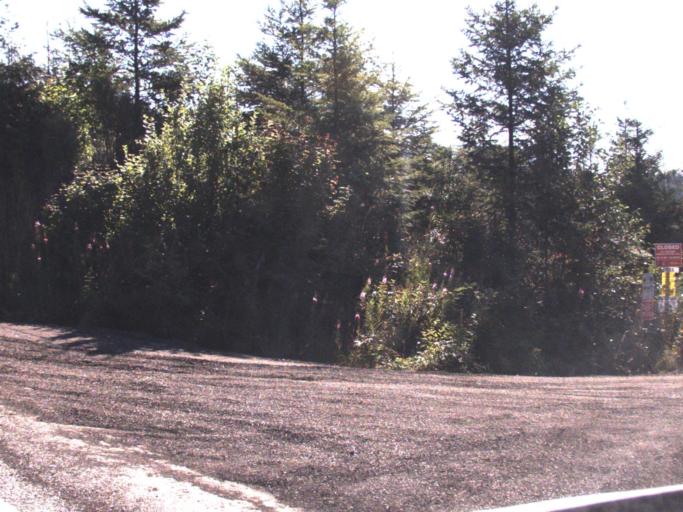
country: US
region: Washington
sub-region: King County
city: Enumclaw
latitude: 47.1734
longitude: -121.8002
